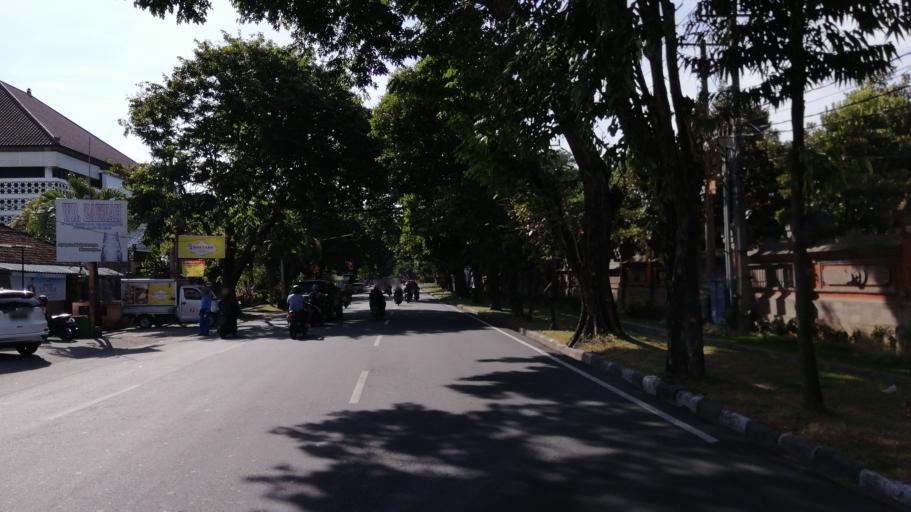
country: ID
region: Bali
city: Denpasar
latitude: -8.6667
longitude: 115.2227
